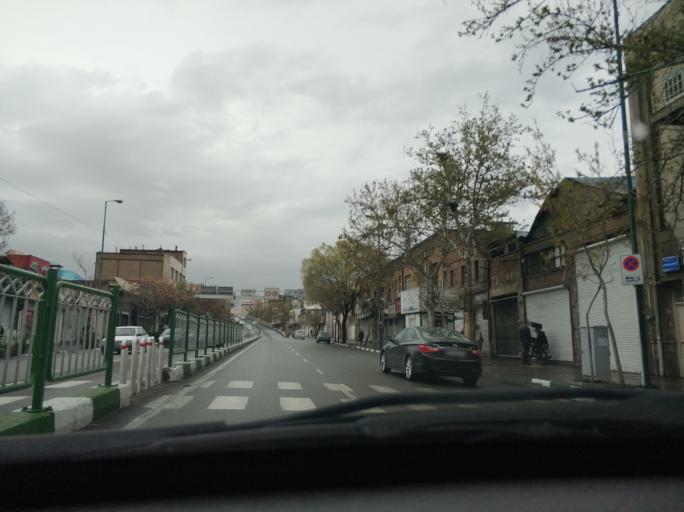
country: IR
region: Tehran
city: Tehran
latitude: 35.6995
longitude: 51.4374
